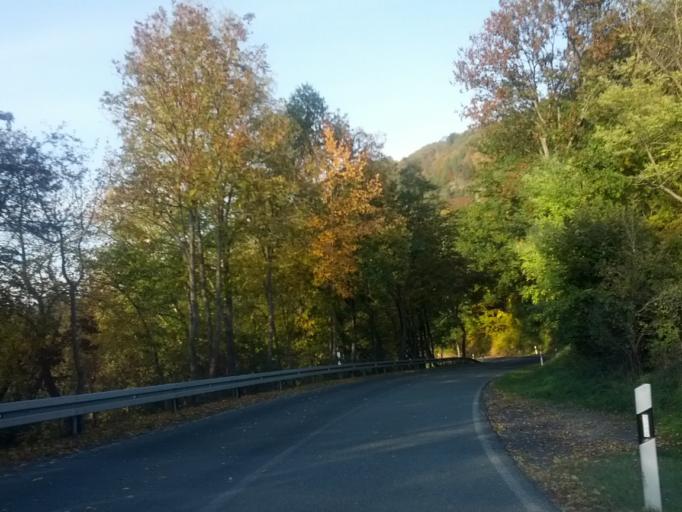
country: DE
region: Thuringia
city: Kahla
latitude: 50.8013
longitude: 11.5982
